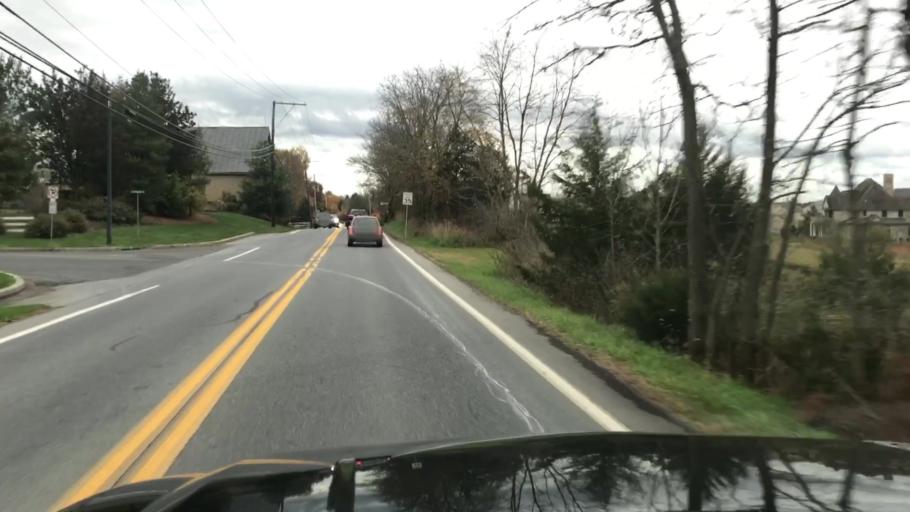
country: US
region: Pennsylvania
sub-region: Cumberland County
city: Shiremanstown
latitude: 40.1701
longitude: -76.9259
